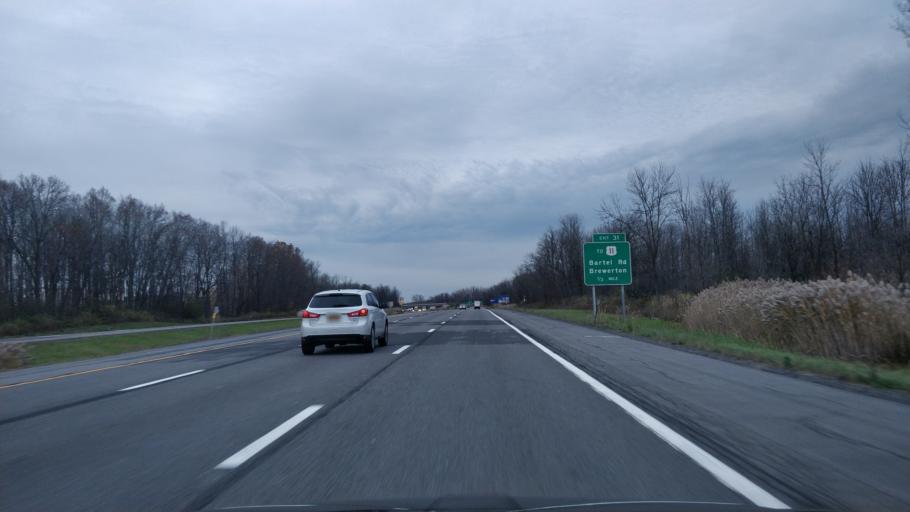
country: US
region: New York
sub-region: Onondaga County
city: Brewerton
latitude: 43.2238
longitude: -76.1291
